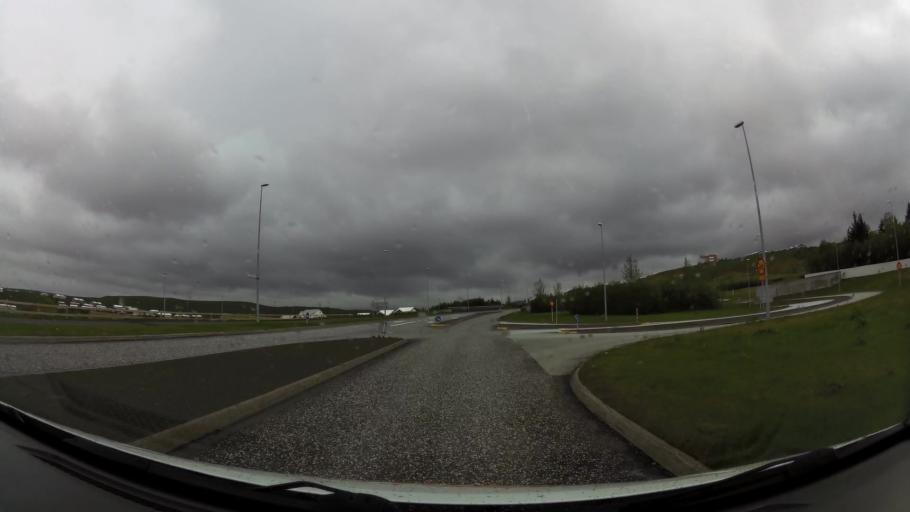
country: IS
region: Capital Region
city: Hafnarfjoerdur
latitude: 64.0617
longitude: -21.9415
